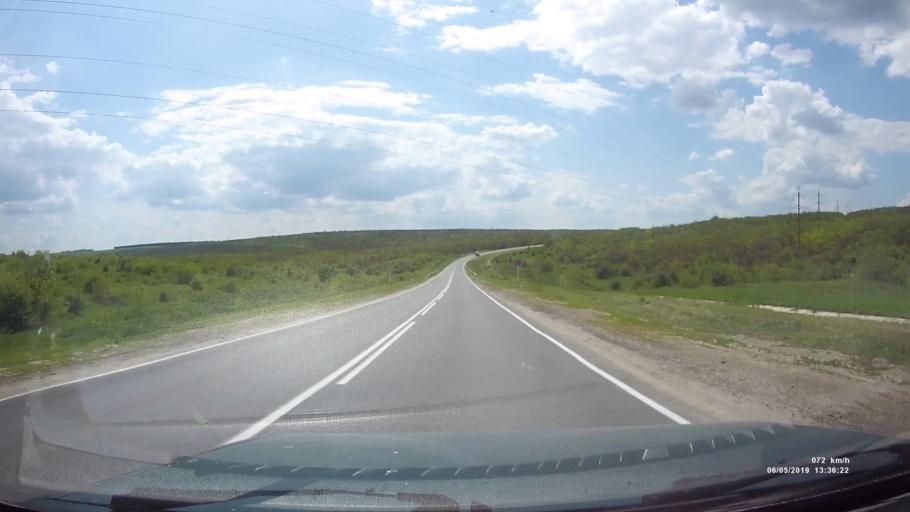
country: RU
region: Rostov
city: Ust'-Donetskiy
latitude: 47.6910
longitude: 40.7330
